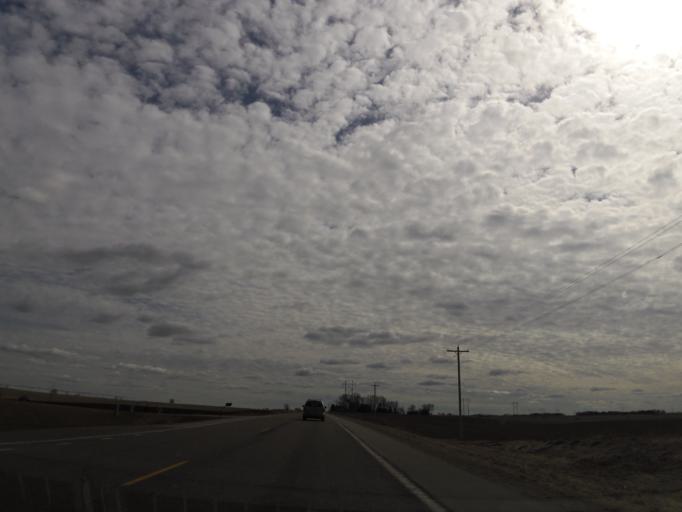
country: US
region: Minnesota
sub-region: Olmsted County
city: Stewartville
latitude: 43.9122
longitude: -92.4085
